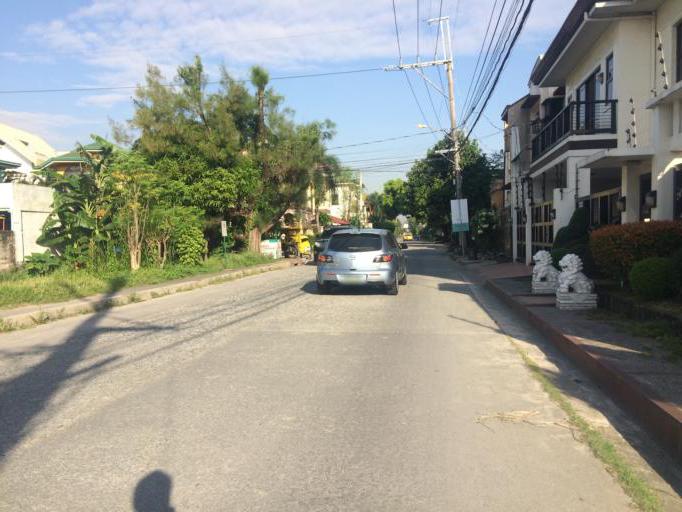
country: PH
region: Calabarzon
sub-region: Province of Rizal
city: Taytay
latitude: 14.5519
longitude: 121.1086
